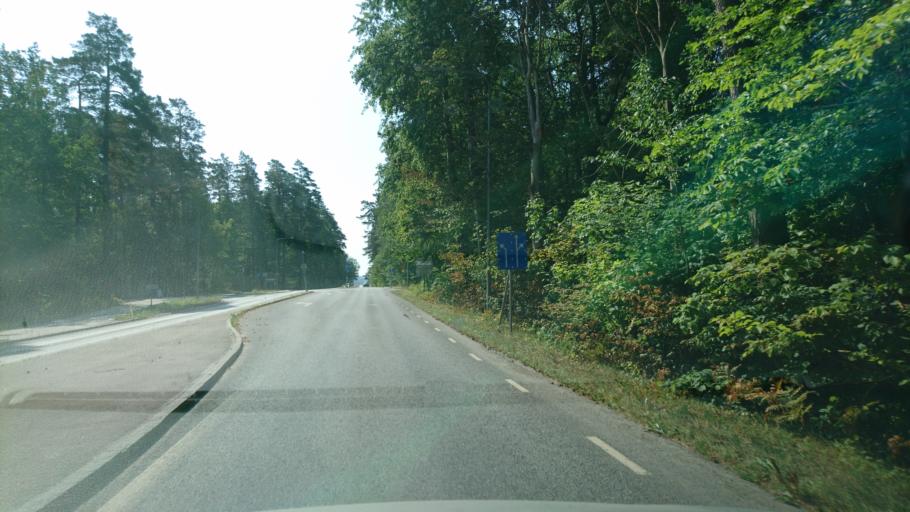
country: SE
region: Uppsala
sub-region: Uppsala Kommun
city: Uppsala
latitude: 59.8287
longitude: 17.6440
